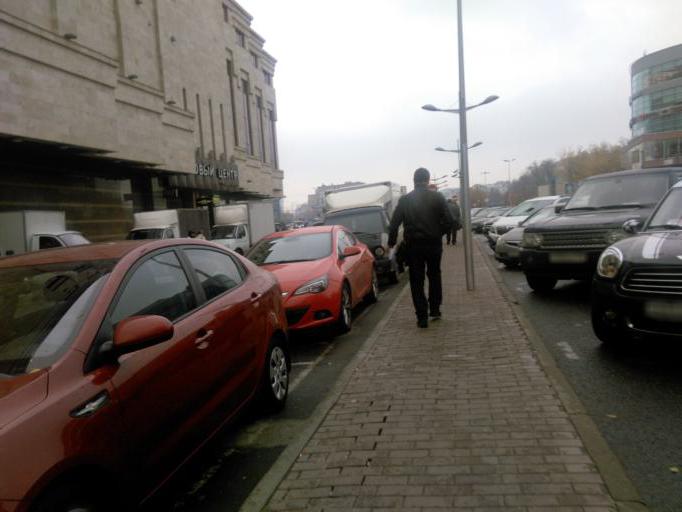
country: RU
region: Moscow
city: Zamoskvorech'ye
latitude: 55.7092
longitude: 37.6228
